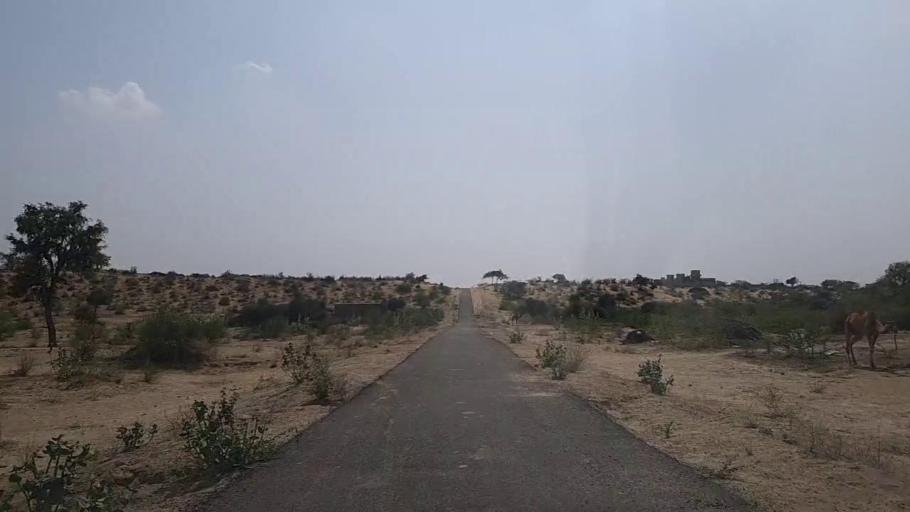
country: PK
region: Sindh
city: Mithi
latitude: 24.7883
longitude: 69.8792
